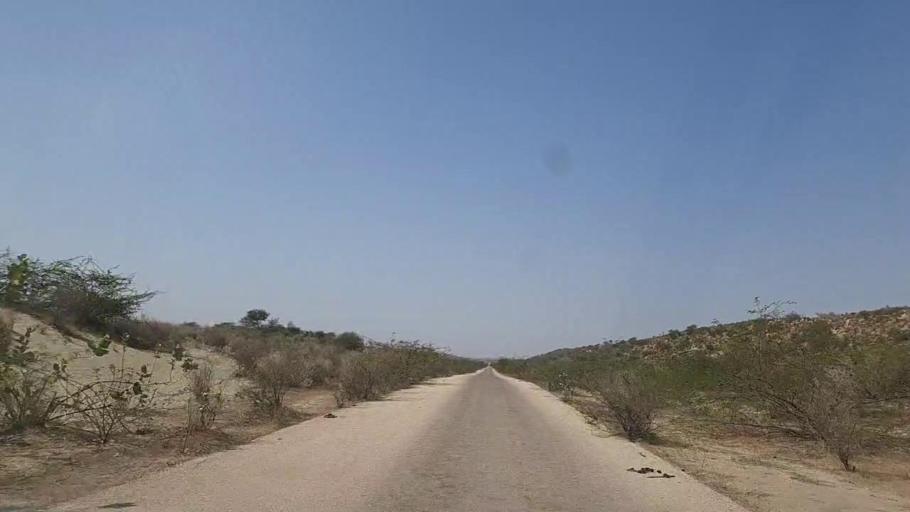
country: PK
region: Sindh
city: Diplo
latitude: 24.5198
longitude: 69.3523
